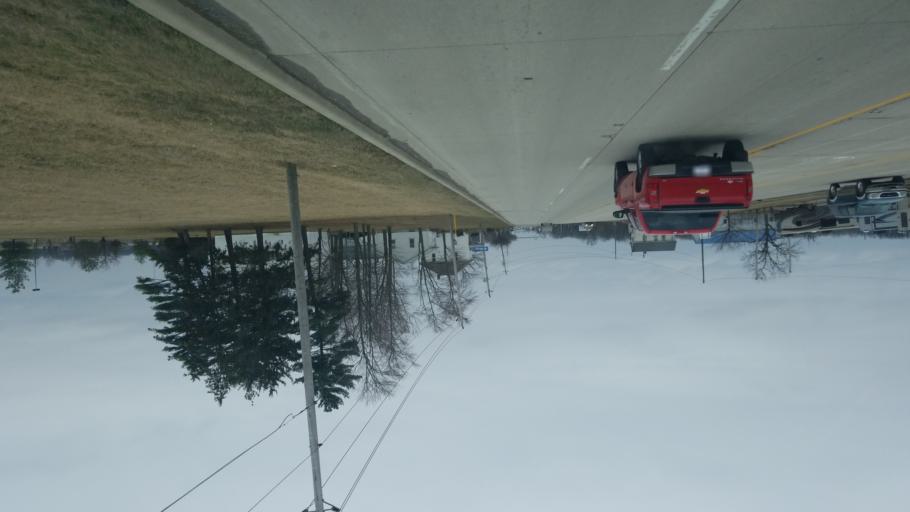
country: US
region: Indiana
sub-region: Adams County
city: Decatur
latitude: 40.8093
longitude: -84.9374
